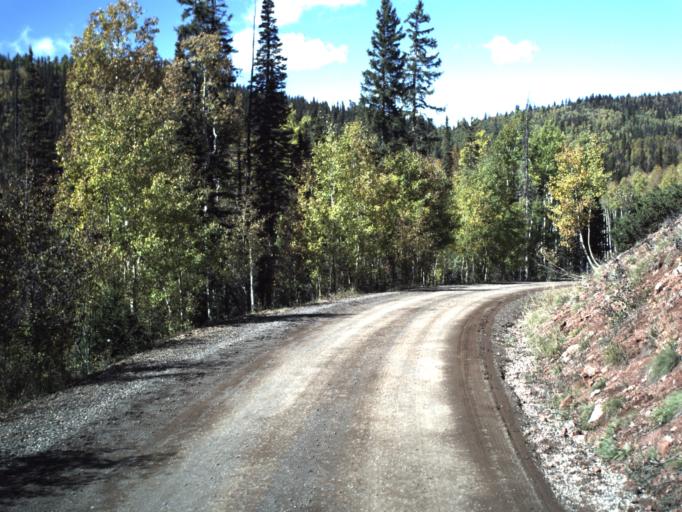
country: US
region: Utah
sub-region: Piute County
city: Junction
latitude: 38.3105
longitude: -112.3644
